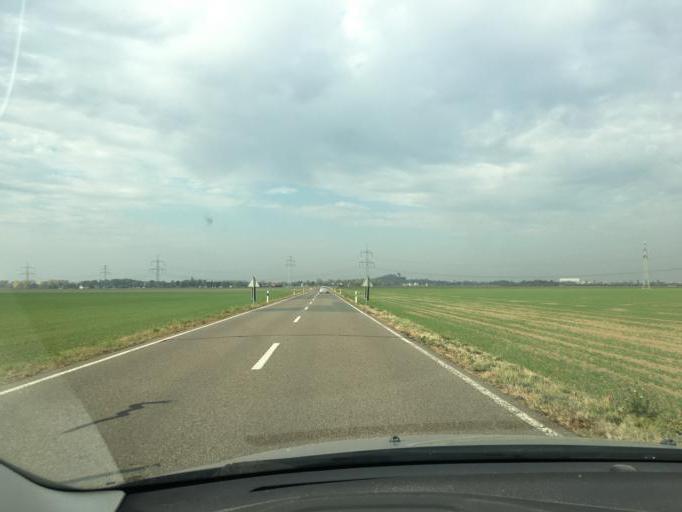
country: DE
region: Saxony-Anhalt
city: Landsberg
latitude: 51.5063
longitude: 12.1905
